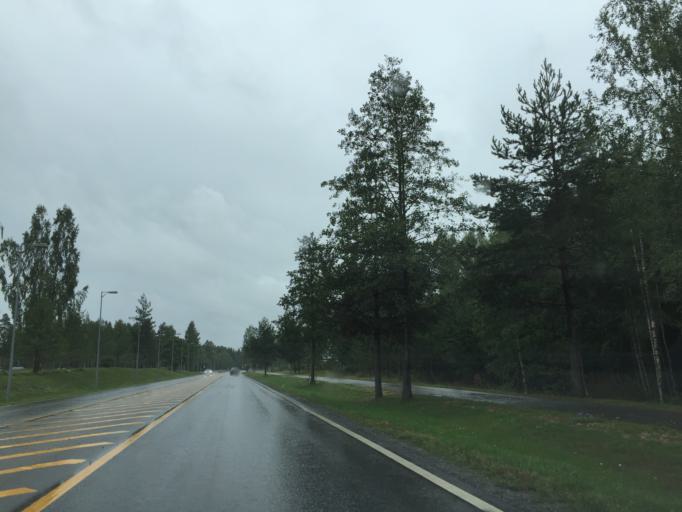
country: NO
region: Akershus
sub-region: Nannestad
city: Teigebyen
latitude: 60.1879
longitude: 11.0905
